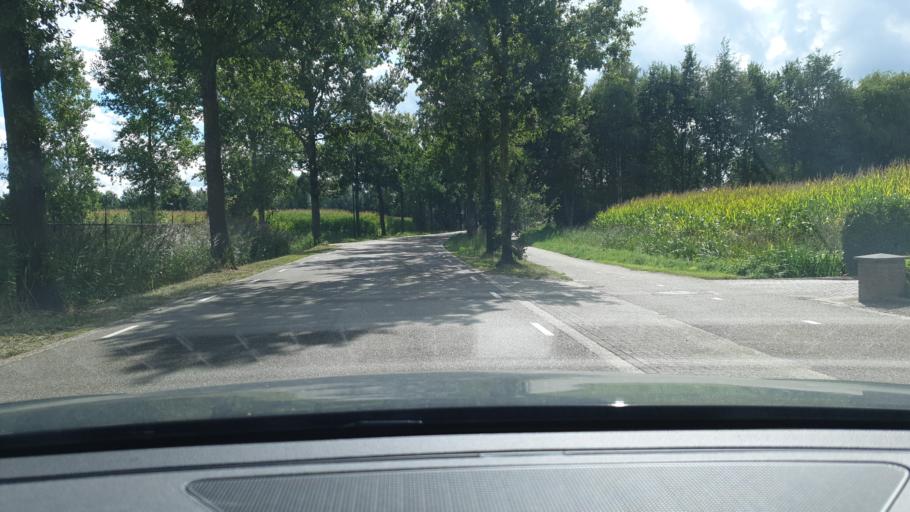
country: NL
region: North Brabant
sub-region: Gemeente Veghel
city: Zijtaart
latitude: 51.5934
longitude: 5.5321
